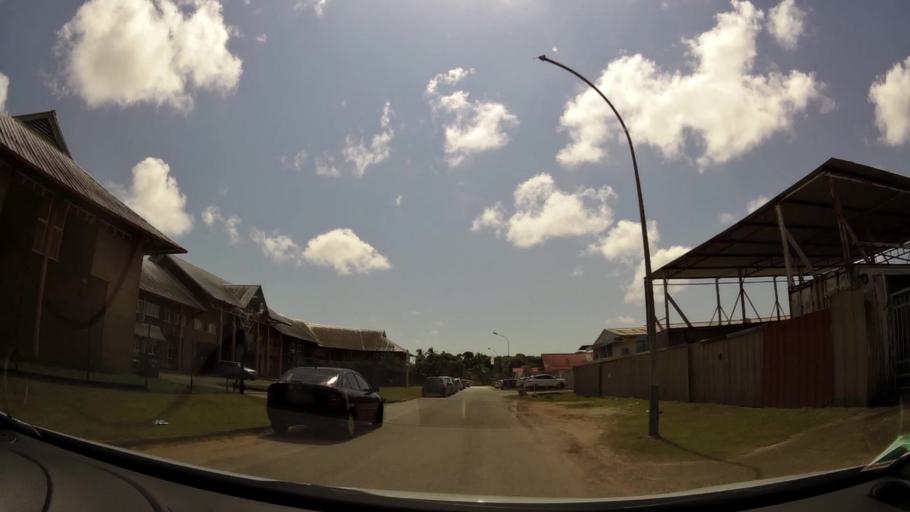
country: GF
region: Guyane
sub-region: Guyane
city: Cayenne
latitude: 4.9289
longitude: -52.3280
